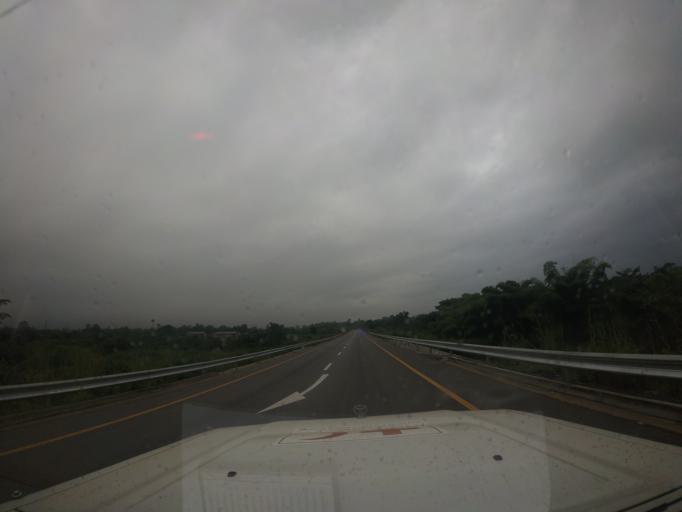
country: SL
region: Eastern Province
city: Hangha
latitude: 7.9430
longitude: -11.1390
